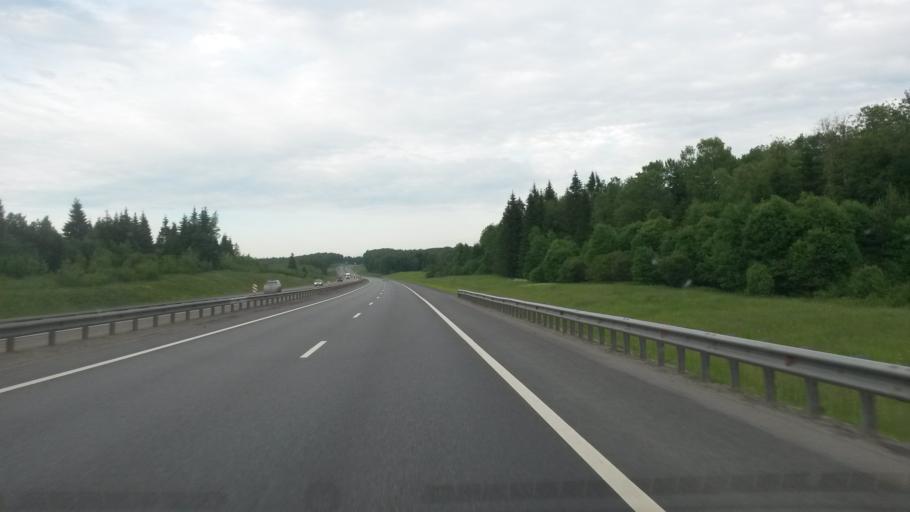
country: RU
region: Vladimir
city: Arsaki
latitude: 56.5002
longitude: 38.4889
